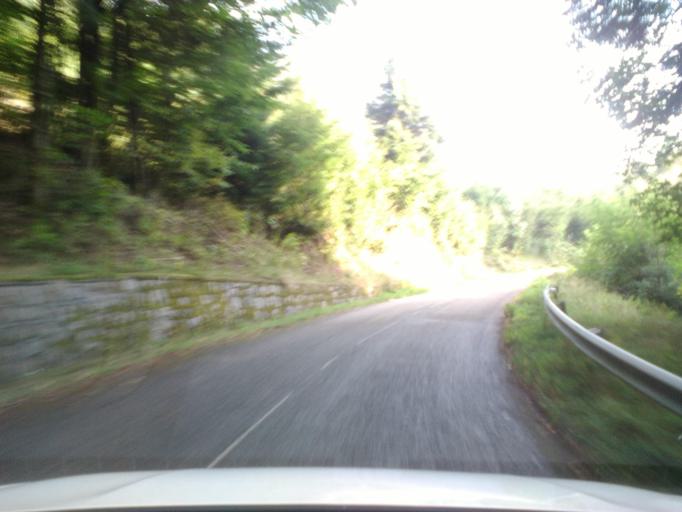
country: FR
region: Lorraine
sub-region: Departement des Vosges
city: Senones
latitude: 48.3855
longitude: 7.0382
